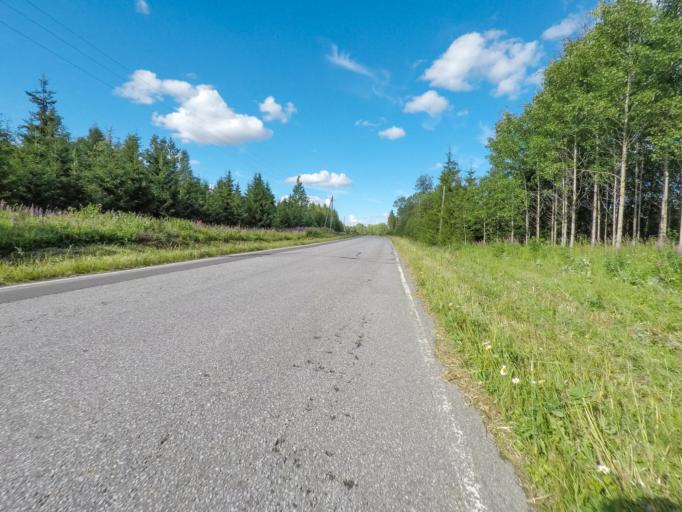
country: FI
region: South Karelia
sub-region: Imatra
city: Imatra
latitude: 61.1375
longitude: 28.7368
